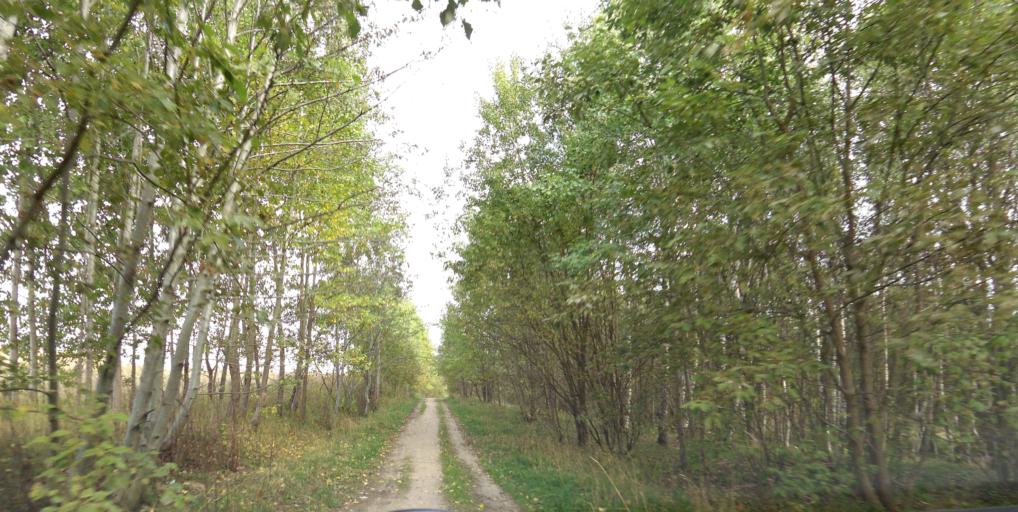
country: LT
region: Vilnius County
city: Justiniskes
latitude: 54.7147
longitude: 25.2095
